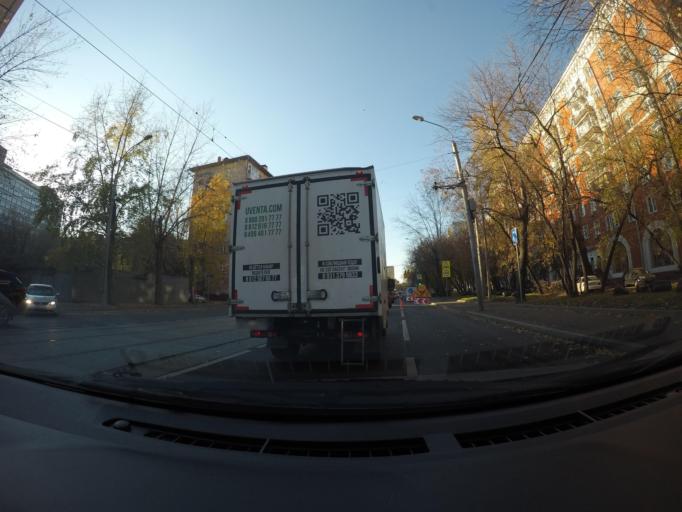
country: RU
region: Moscow
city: Rostokino
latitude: 55.8225
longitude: 37.6599
